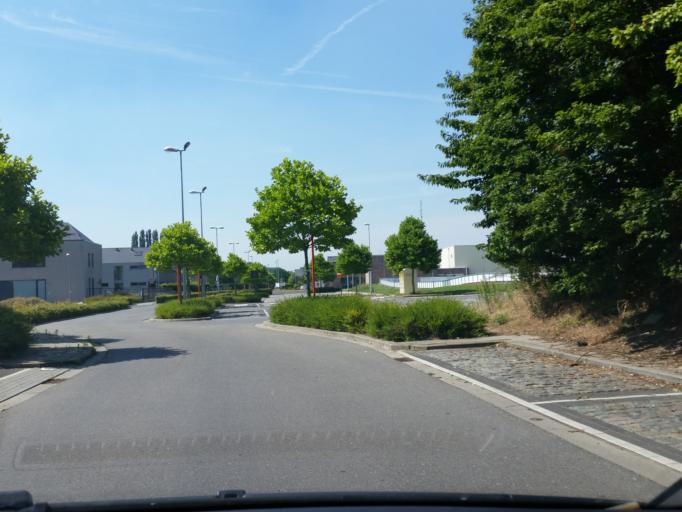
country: BE
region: Flanders
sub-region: Provincie Vlaams-Brabant
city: Zemst
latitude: 50.9706
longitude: 4.4499
